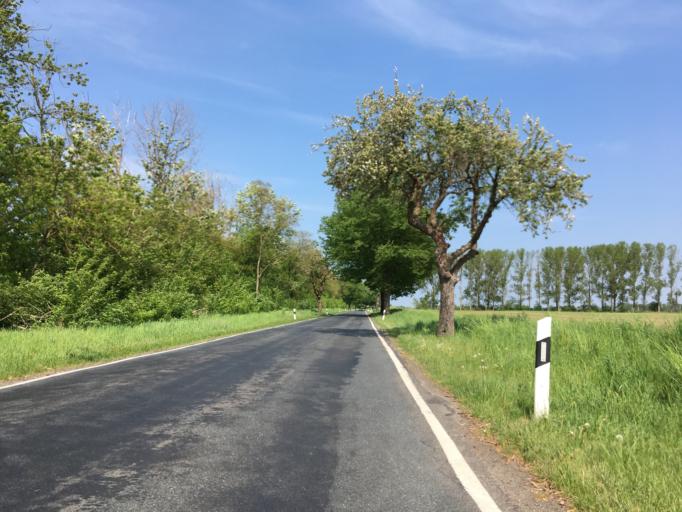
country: DE
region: Brandenburg
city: Werneuchen
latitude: 52.6923
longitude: 13.7254
